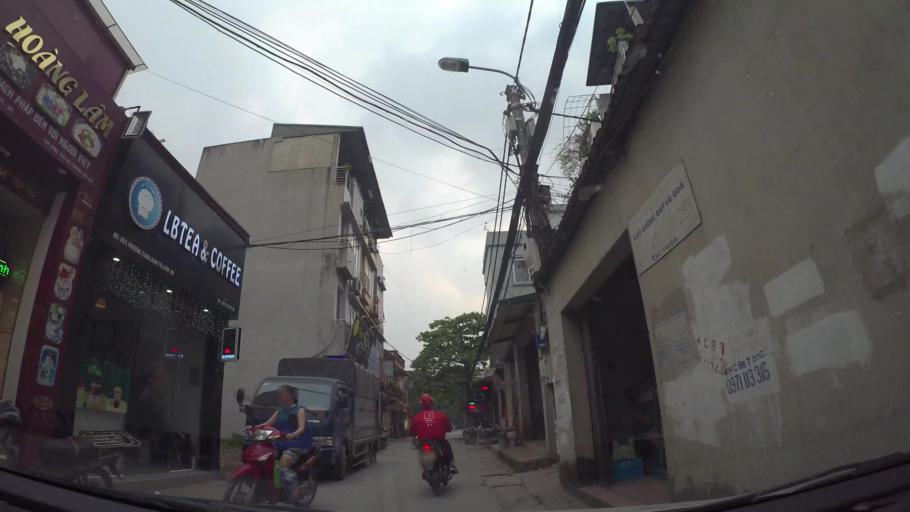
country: VN
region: Ha Noi
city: Cau Dien
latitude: 21.0348
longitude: 105.7410
